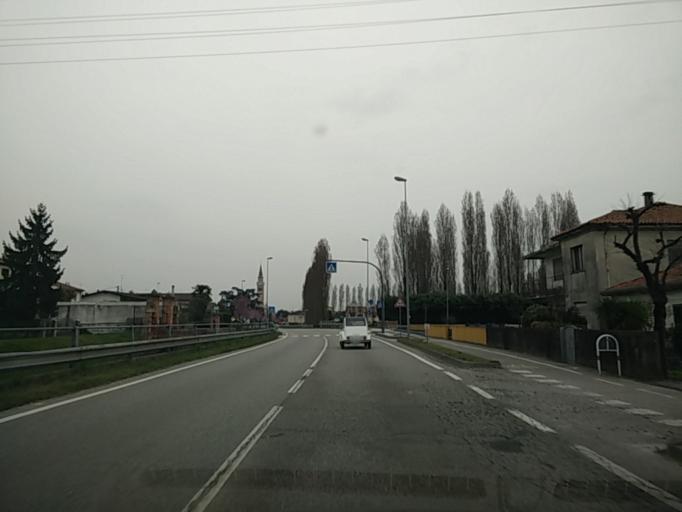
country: IT
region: Veneto
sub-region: Provincia di Venezia
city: Moniego
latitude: 45.5616
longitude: 12.0773
